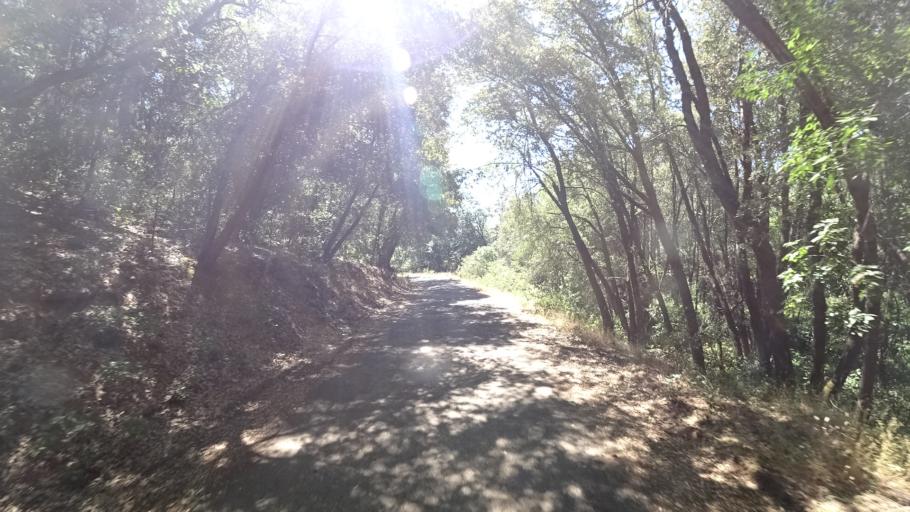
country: US
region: California
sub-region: Calaveras County
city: Forest Meadows
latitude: 38.1738
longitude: -120.3744
